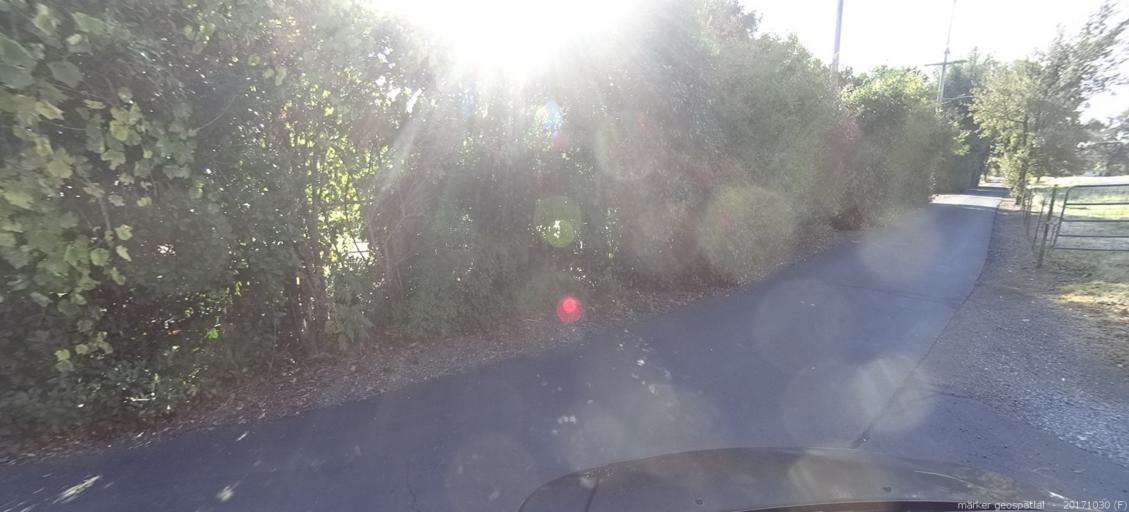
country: US
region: California
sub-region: Shasta County
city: Palo Cedro
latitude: 40.5637
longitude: -122.2010
